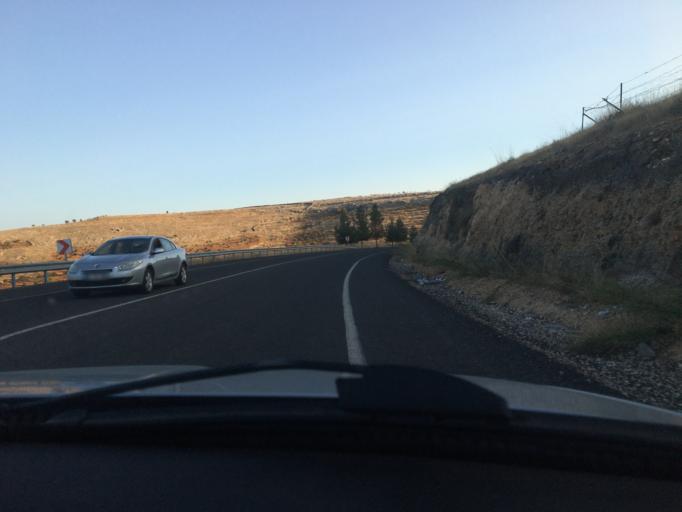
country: TR
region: Sanliurfa
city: Halfeti
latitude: 37.2258
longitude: 37.9589
